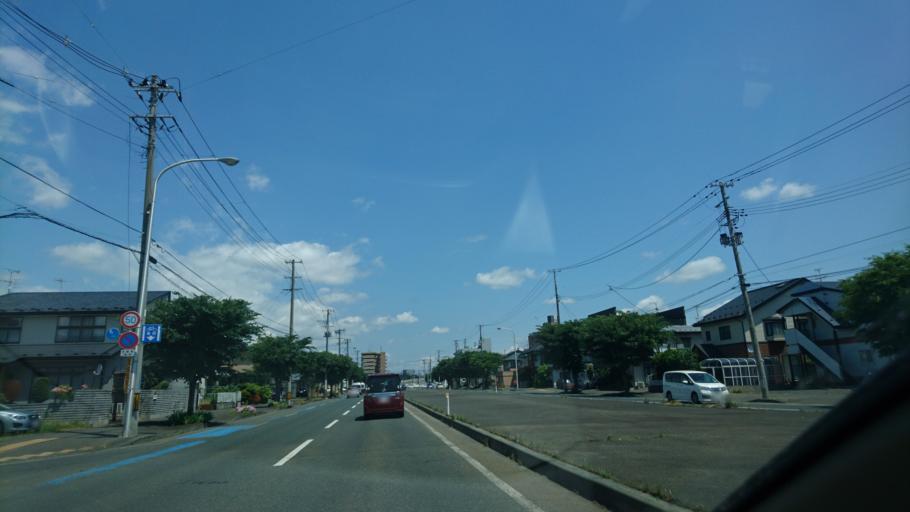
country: JP
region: Iwate
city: Morioka-shi
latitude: 39.6863
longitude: 141.1355
